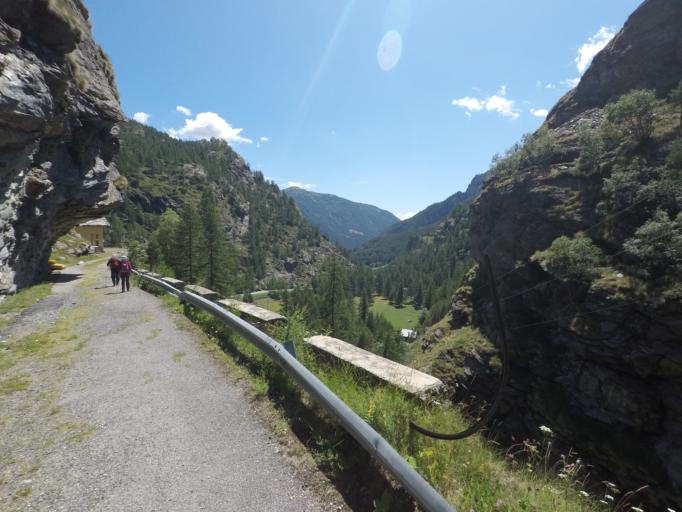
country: IT
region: Aosta Valley
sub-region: Valle d'Aosta
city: Paquier
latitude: 45.9046
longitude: 7.6161
